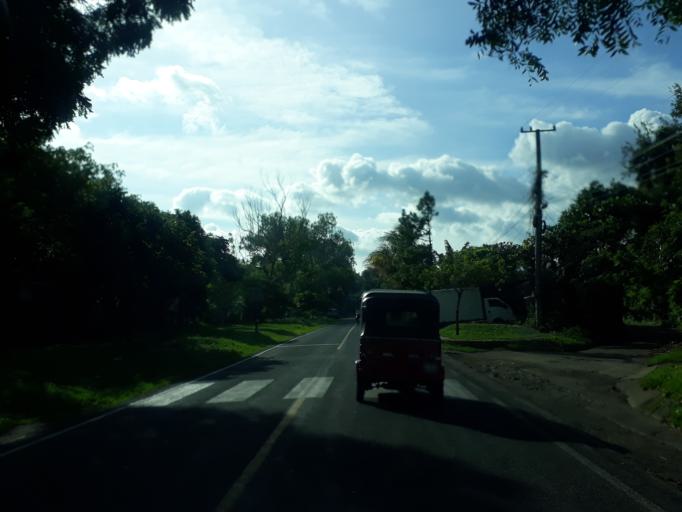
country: NI
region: Carazo
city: San Marcos
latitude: 11.9069
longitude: -86.1838
